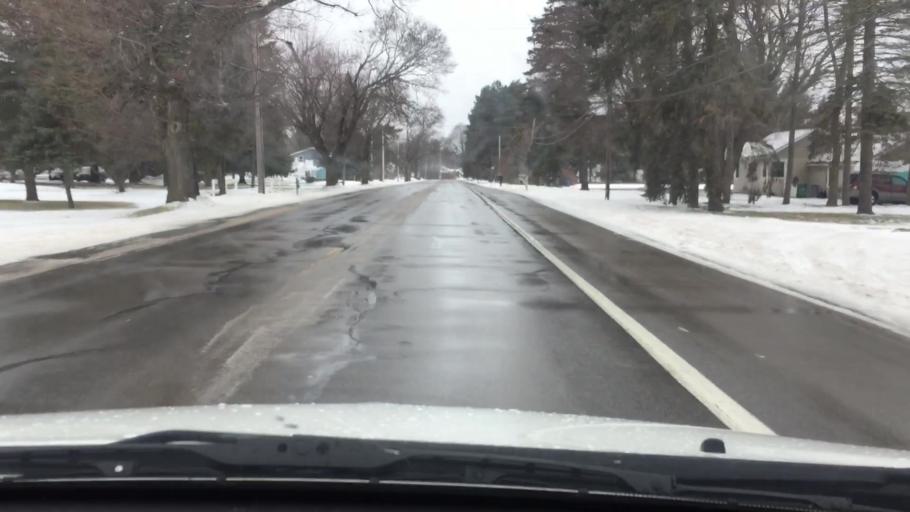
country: US
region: Michigan
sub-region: Wexford County
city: Cadillac
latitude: 44.2339
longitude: -85.4188
